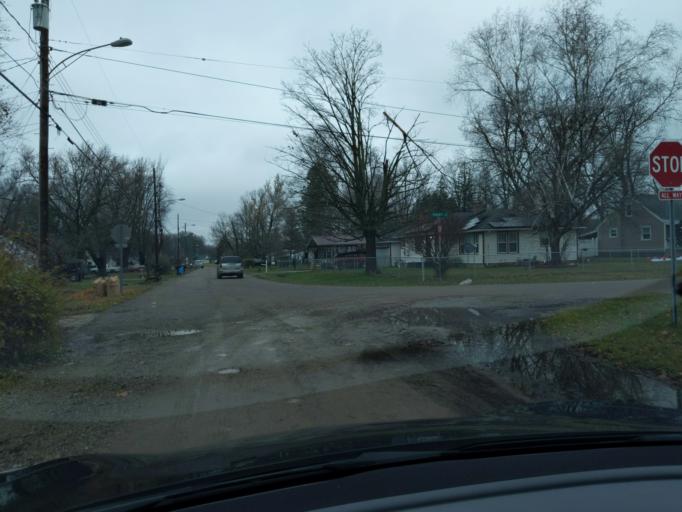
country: US
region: Michigan
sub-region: Ingham County
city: Lansing
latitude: 42.6805
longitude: -84.5714
